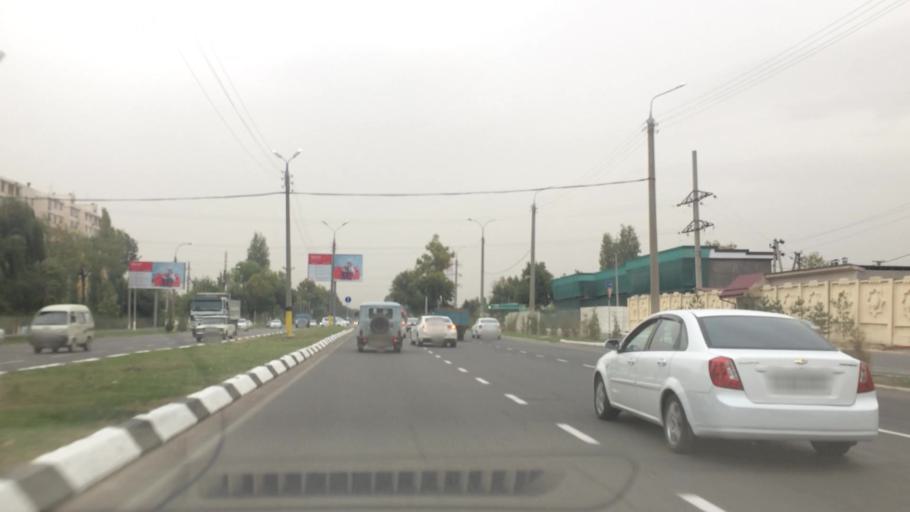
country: UZ
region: Toshkent
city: Salor
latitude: 41.3189
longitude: 69.3590
